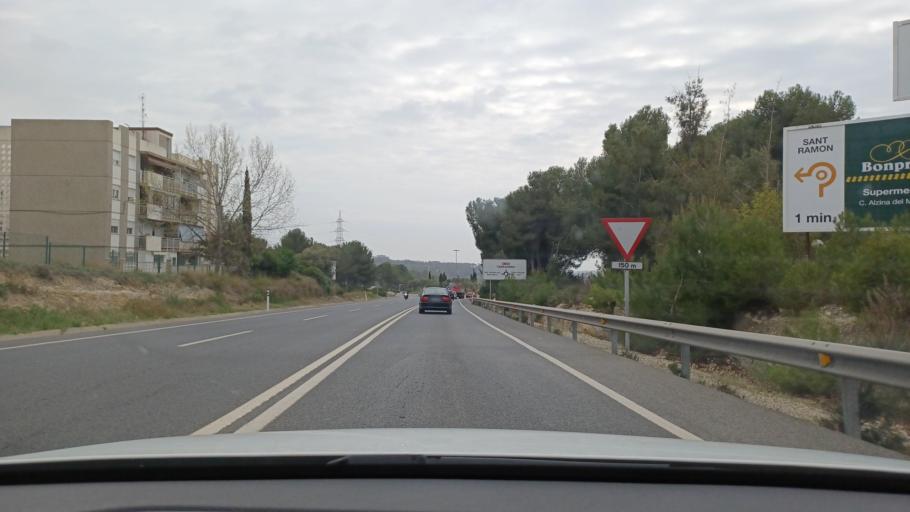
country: ES
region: Catalonia
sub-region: Provincia de Tarragona
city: Constanti
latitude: 41.1547
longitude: 1.2400
